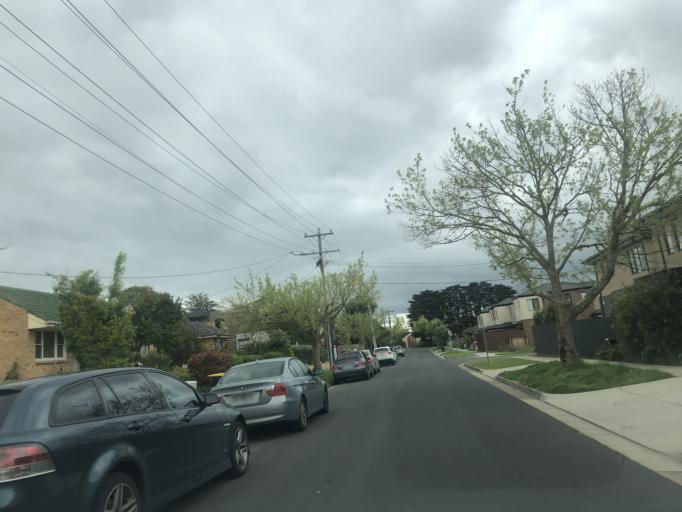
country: AU
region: Victoria
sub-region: Greater Dandenong
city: Dandenong North
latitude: -37.9801
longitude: 145.2231
